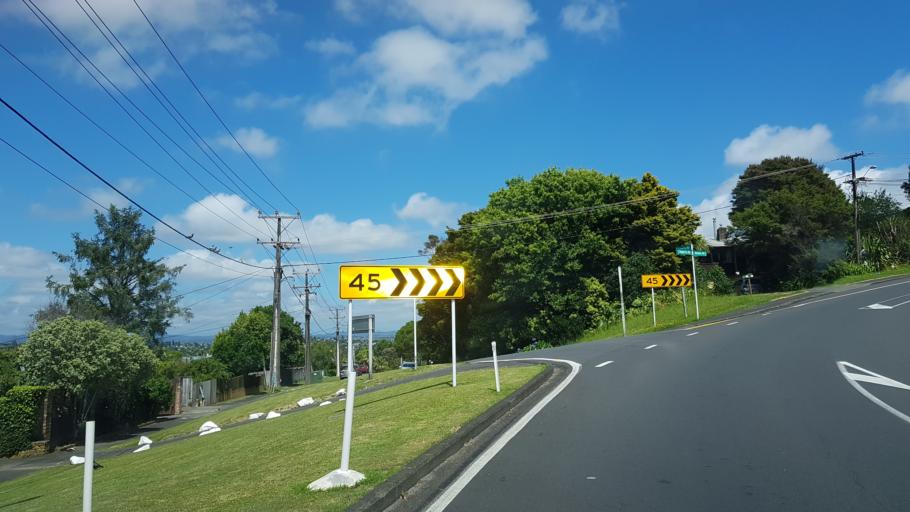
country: NZ
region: Auckland
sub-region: Auckland
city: North Shore
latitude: -36.7904
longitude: 174.7183
